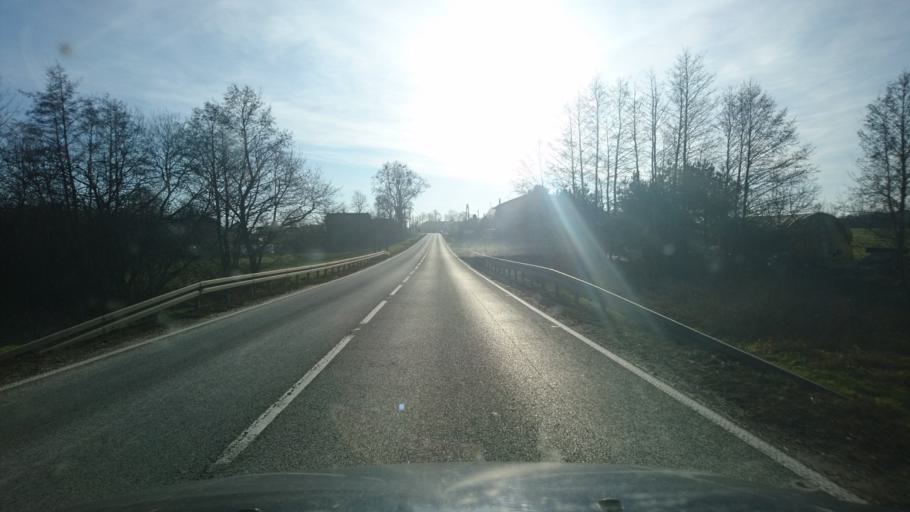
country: PL
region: Opole Voivodeship
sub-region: Powiat oleski
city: Dalachow
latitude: 51.0468
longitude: 18.5972
